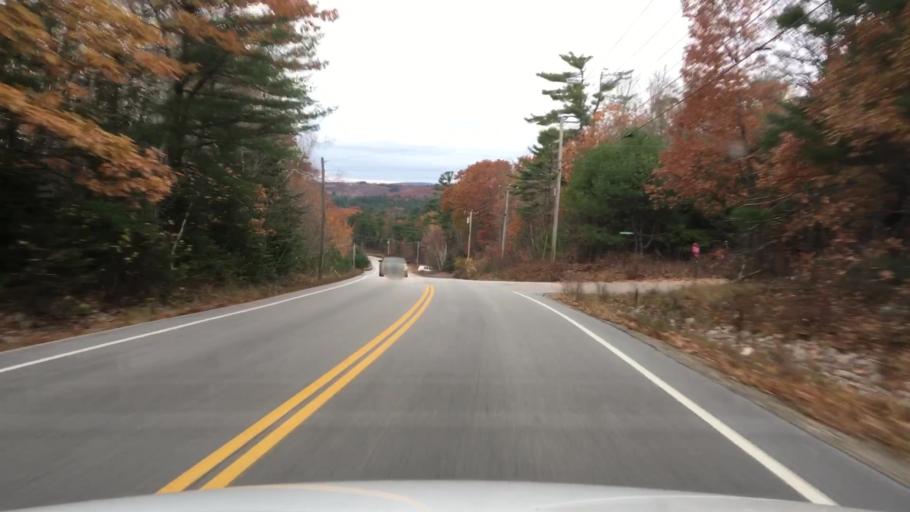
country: US
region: Maine
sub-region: Hancock County
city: Orland
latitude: 44.5548
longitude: -68.6952
